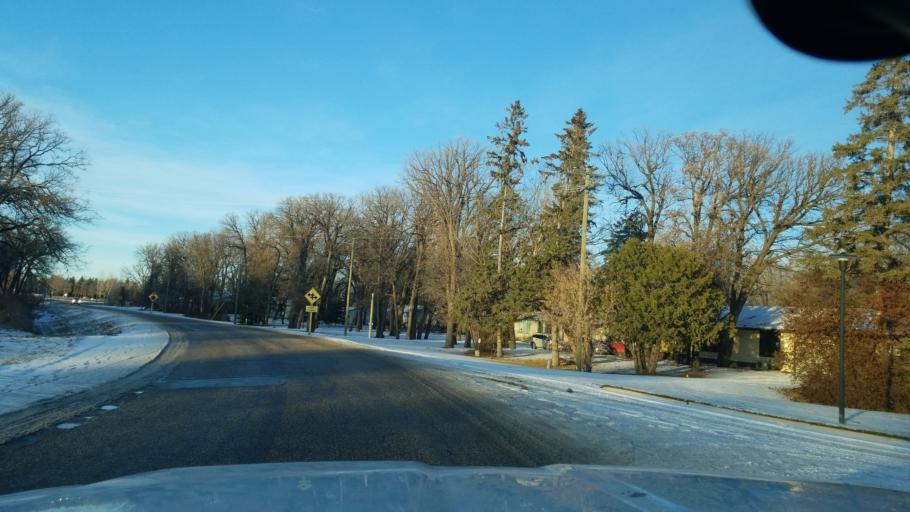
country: CA
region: Manitoba
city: Portage la Prairie
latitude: 49.9512
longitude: -98.3275
